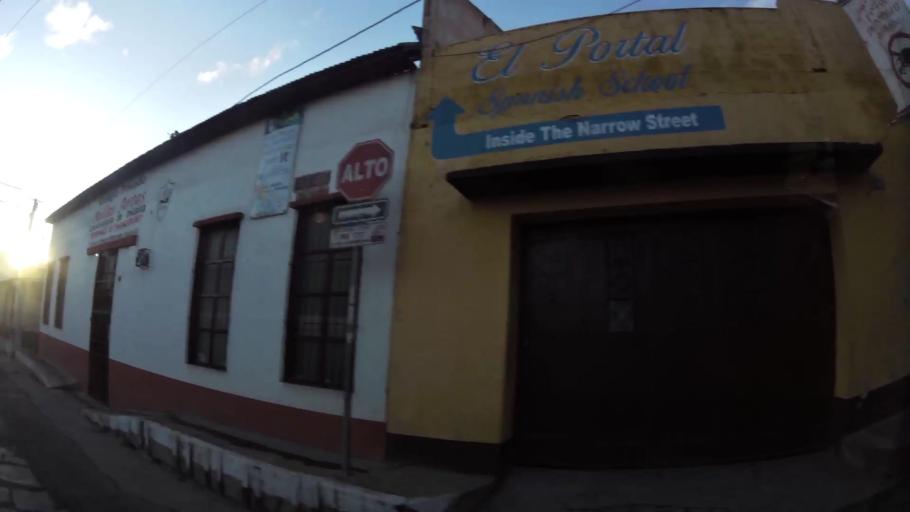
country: GT
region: Quetzaltenango
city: Quetzaltenango
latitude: 14.8313
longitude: -91.5197
